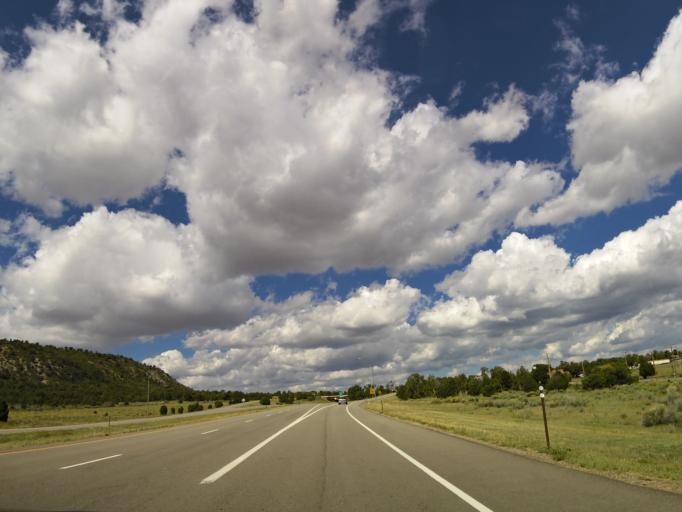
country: US
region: Colorado
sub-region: Montezuma County
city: Mancos
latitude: 37.3393
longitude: -108.4063
